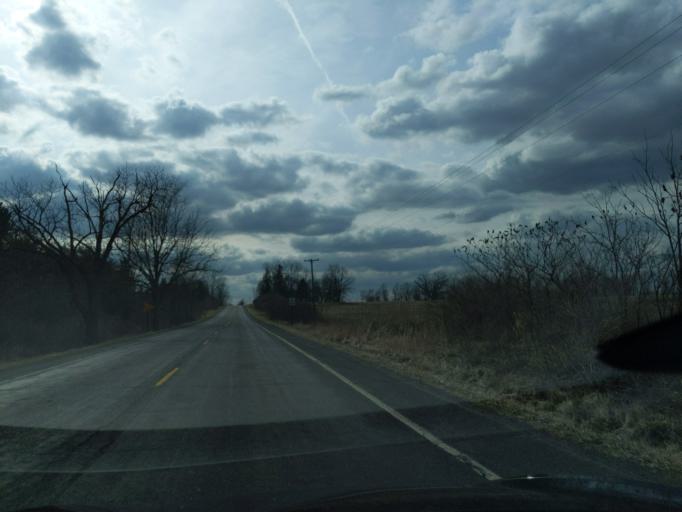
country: US
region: Michigan
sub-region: Ingham County
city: Mason
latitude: 42.5241
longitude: -84.4534
